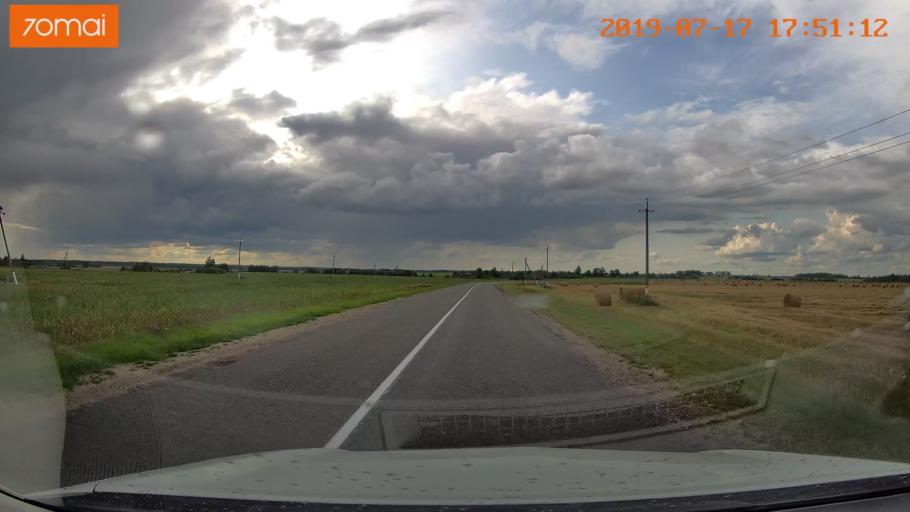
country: BY
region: Mogilev
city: Hlusha
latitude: 53.1492
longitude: 28.7908
